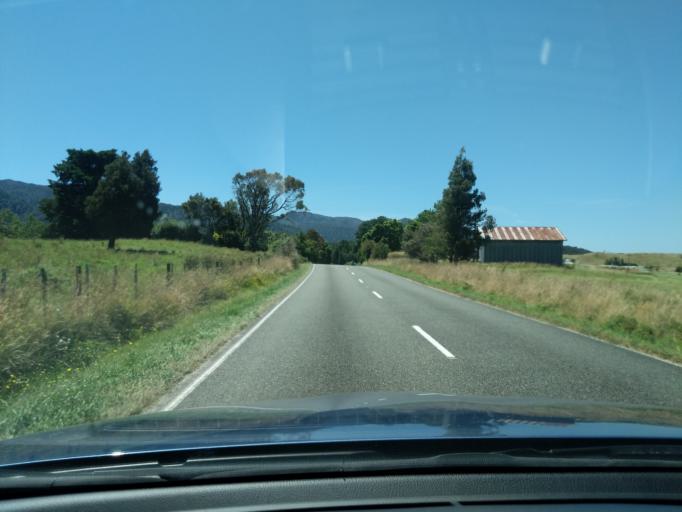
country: NZ
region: Tasman
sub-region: Tasman District
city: Takaka
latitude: -40.7514
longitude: 172.5625
